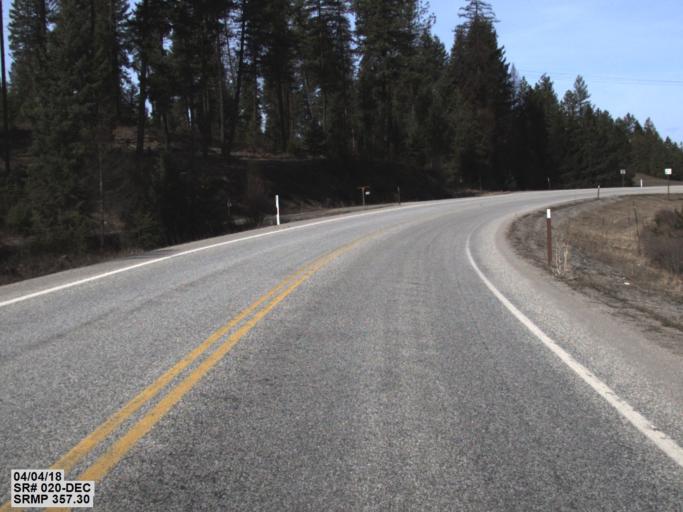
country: US
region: Washington
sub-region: Stevens County
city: Colville
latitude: 48.5413
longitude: -117.8451
